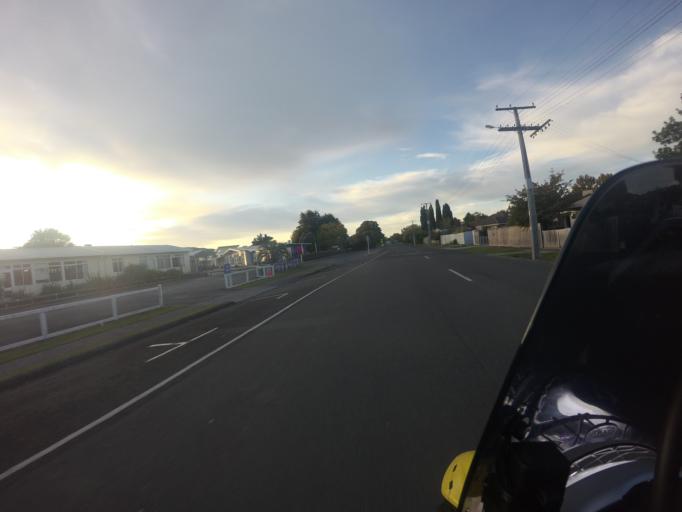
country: NZ
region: Gisborne
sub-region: Gisborne District
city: Gisborne
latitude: -38.6682
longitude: 178.0422
